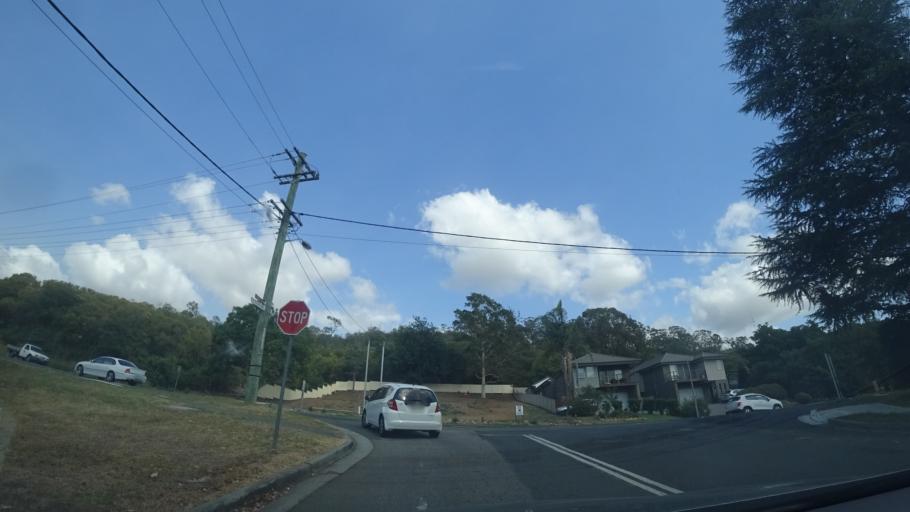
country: AU
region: New South Wales
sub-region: Wollondilly
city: Picton
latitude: -34.1803
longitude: 150.6085
